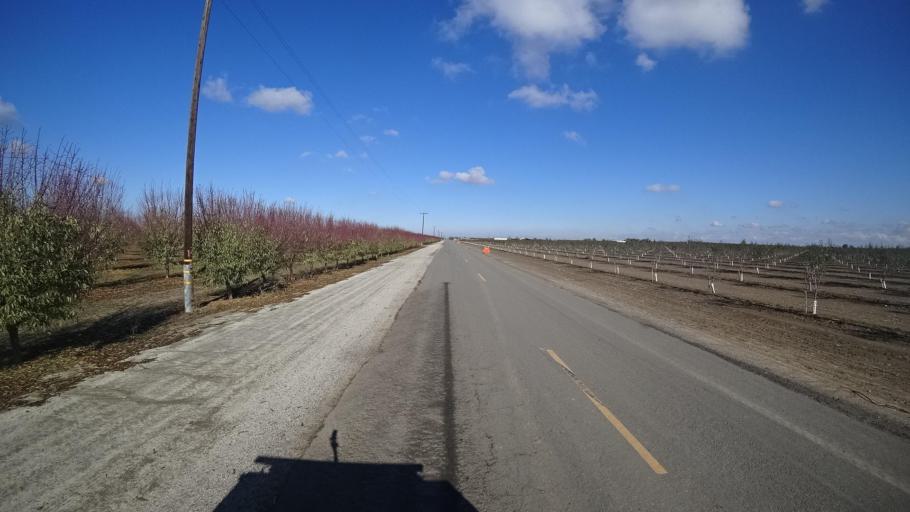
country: US
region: California
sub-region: Kern County
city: McFarland
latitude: 35.6627
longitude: -119.2588
